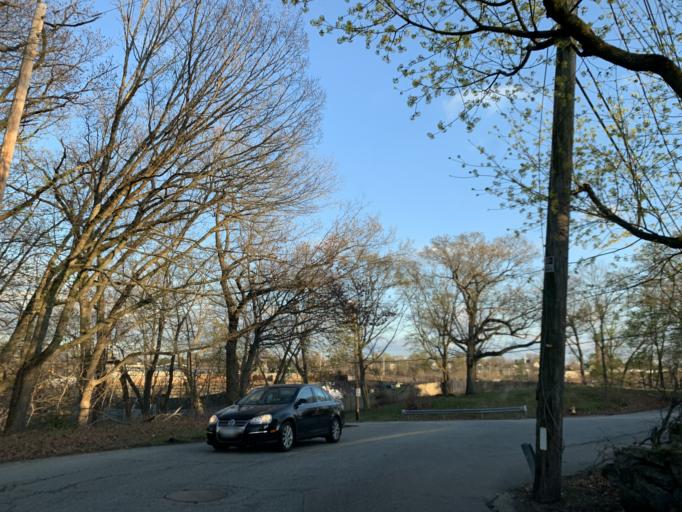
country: US
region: Rhode Island
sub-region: Providence County
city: Valley Falls
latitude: 41.8984
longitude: -71.3769
